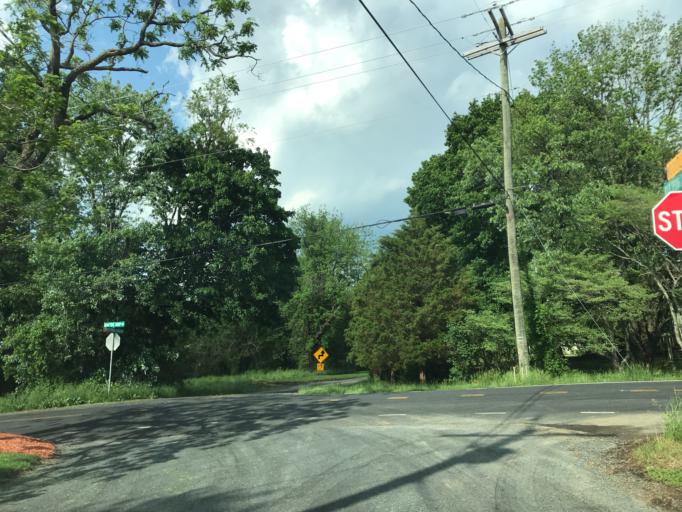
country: US
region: Maryland
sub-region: Harford County
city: Bel Air North
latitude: 39.5747
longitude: -76.4004
